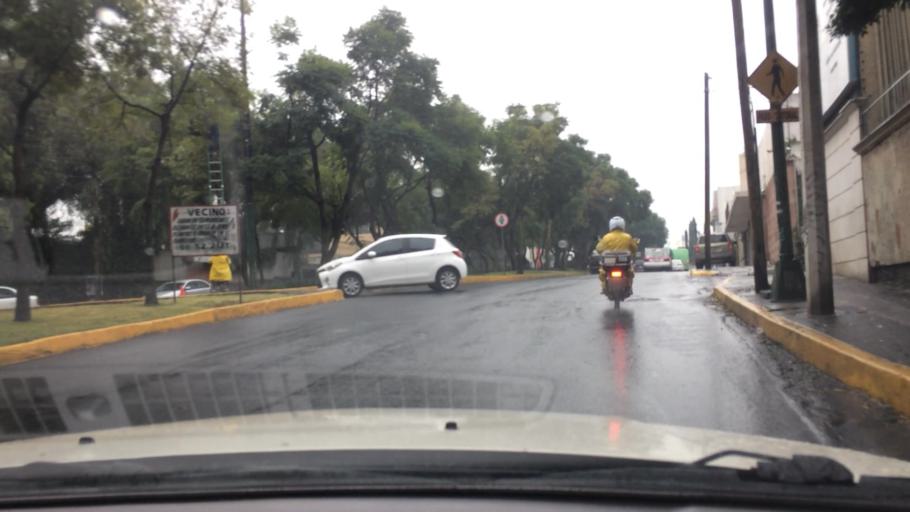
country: MX
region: Mexico City
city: Magdalena Contreras
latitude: 19.3327
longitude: -99.2001
